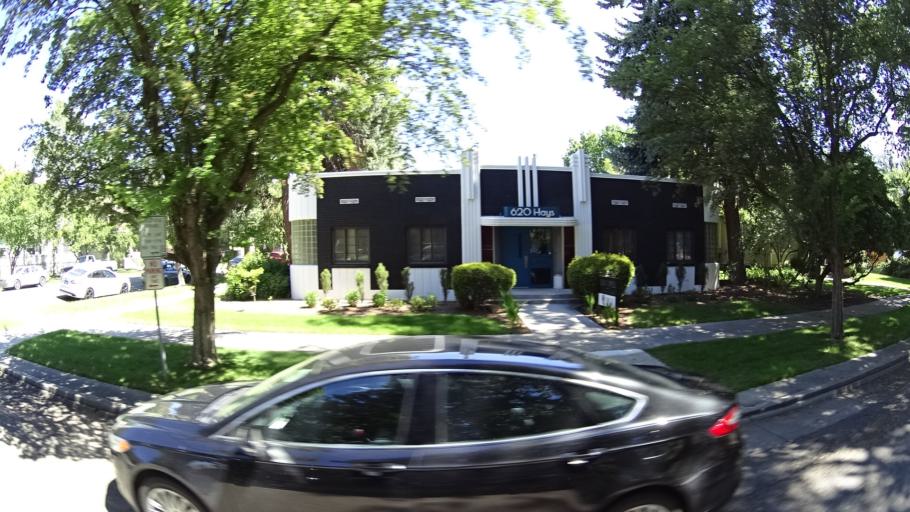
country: US
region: Idaho
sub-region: Ada County
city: Boise
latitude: 43.6202
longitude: -116.1969
